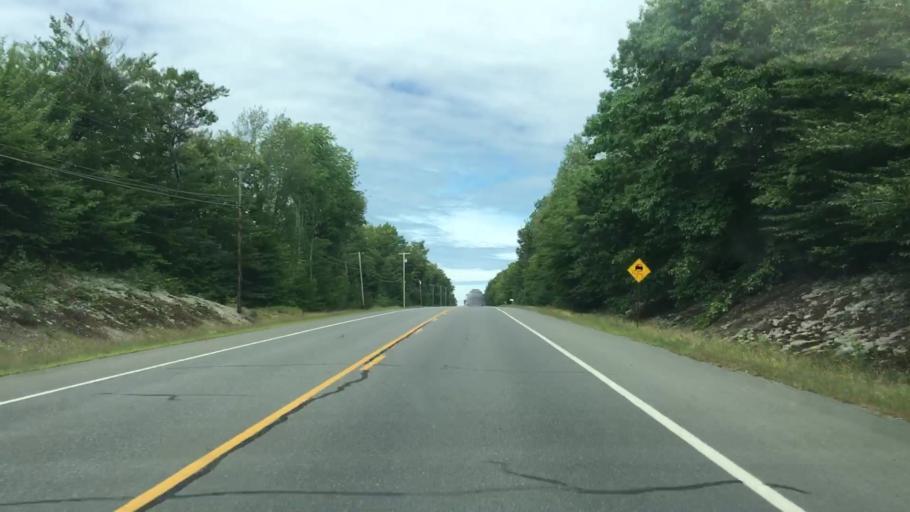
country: US
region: Maine
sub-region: Piscataquis County
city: Brownville
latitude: 45.2808
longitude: -69.0091
